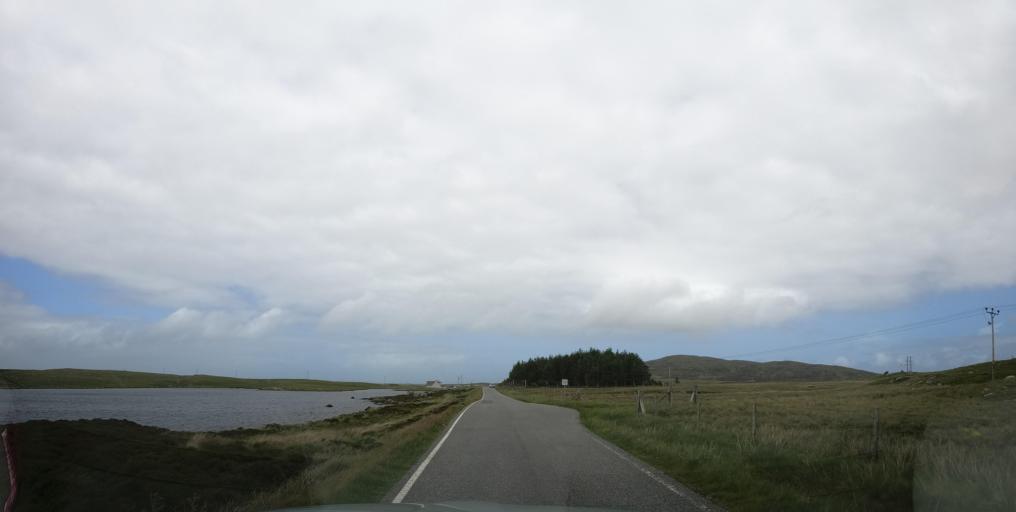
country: GB
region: Scotland
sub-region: Eilean Siar
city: Isle of South Uist
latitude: 57.2841
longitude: -7.3663
